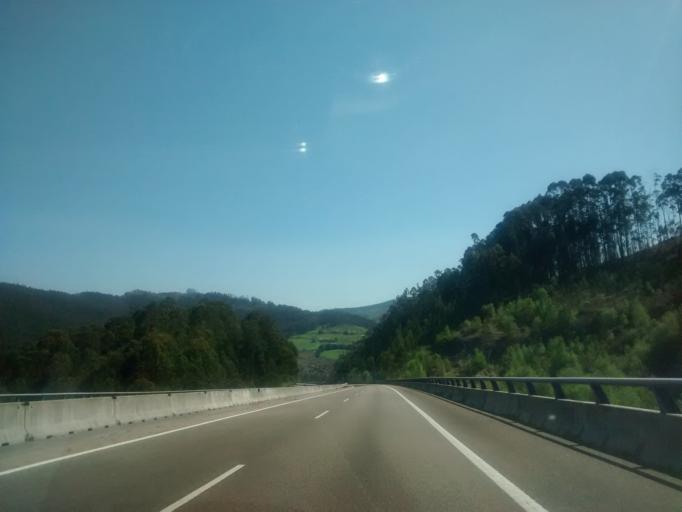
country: ES
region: Asturias
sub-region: Province of Asturias
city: Arriba
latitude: 43.5046
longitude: -5.5437
